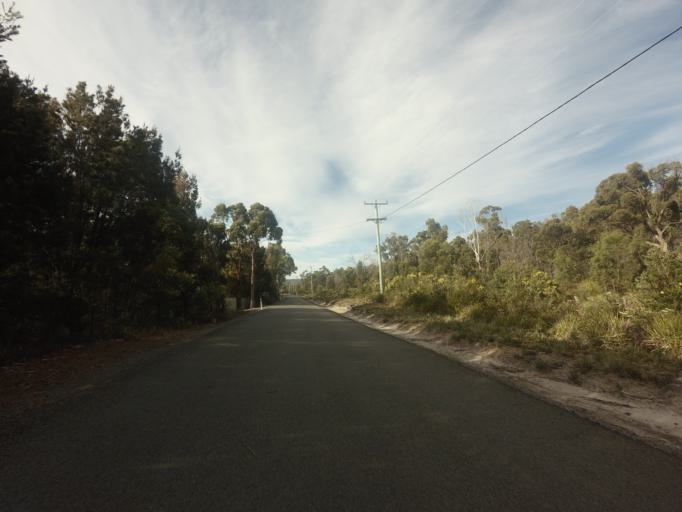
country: AU
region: Tasmania
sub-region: Sorell
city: Sorell
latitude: -42.9604
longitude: 147.8388
